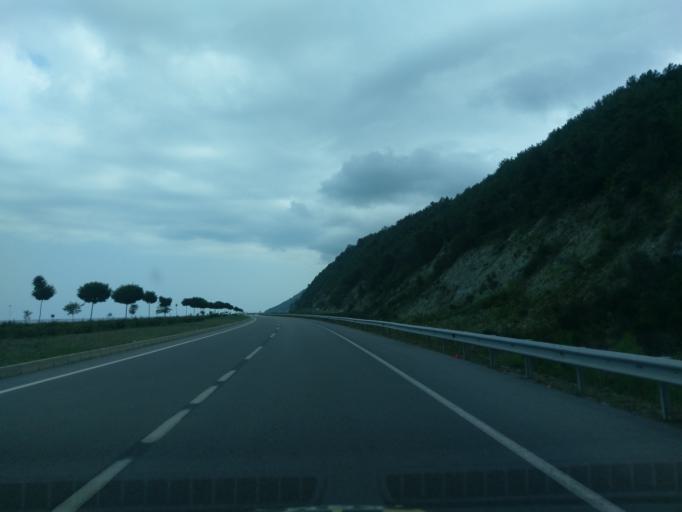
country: TR
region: Sinop
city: Dikmen
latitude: 41.7088
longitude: 35.2958
